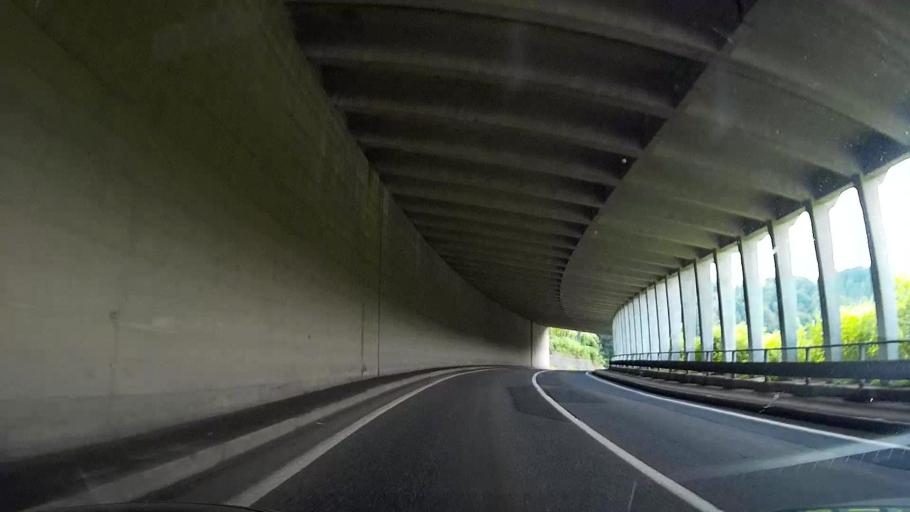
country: JP
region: Niigata
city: Tokamachi
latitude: 36.9932
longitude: 138.6105
